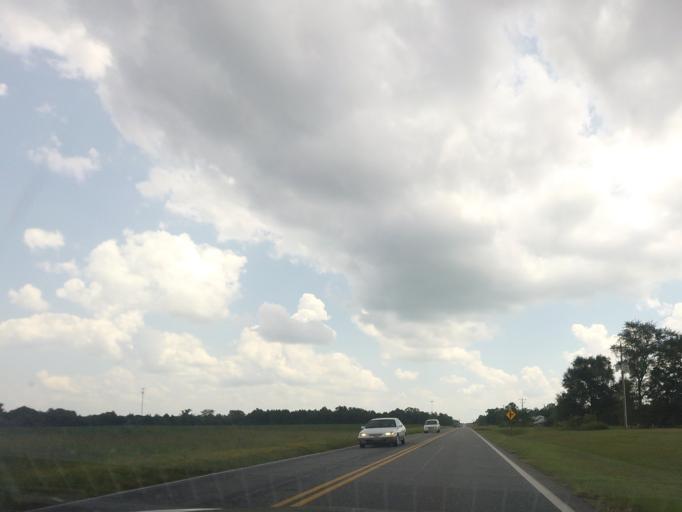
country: US
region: Georgia
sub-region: Bleckley County
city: Cochran
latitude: 32.4150
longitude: -83.3511
